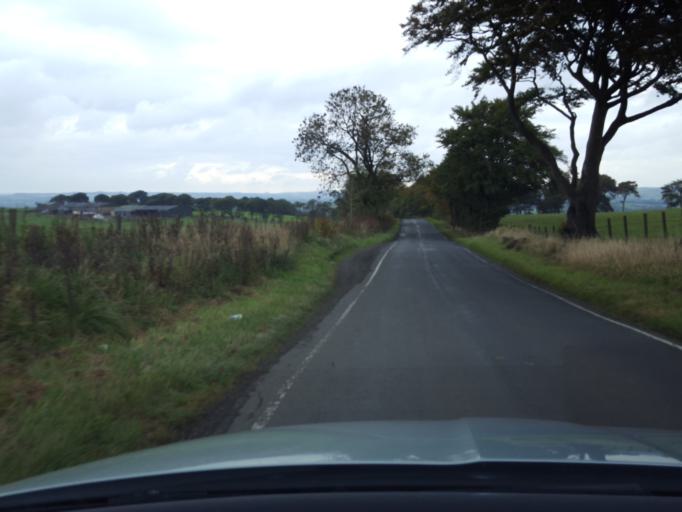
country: GB
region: Scotland
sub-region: West Lothian
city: Bathgate
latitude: 55.9108
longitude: -3.6144
